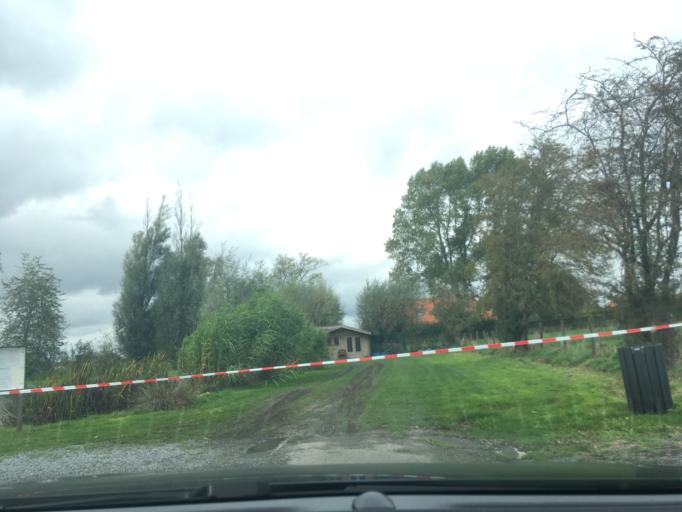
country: BE
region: Flanders
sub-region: Provincie West-Vlaanderen
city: Moorslede
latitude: 50.8893
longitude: 3.0521
